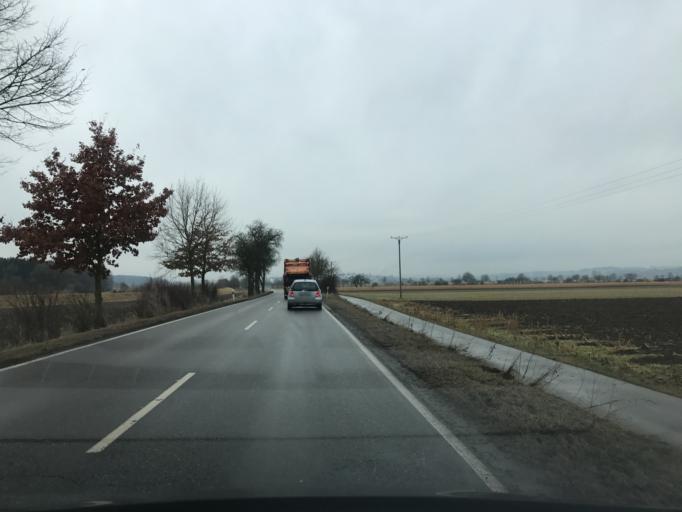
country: DE
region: Baden-Wuerttemberg
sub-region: Tuebingen Region
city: Opfingen
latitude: 48.2705
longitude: 9.8188
